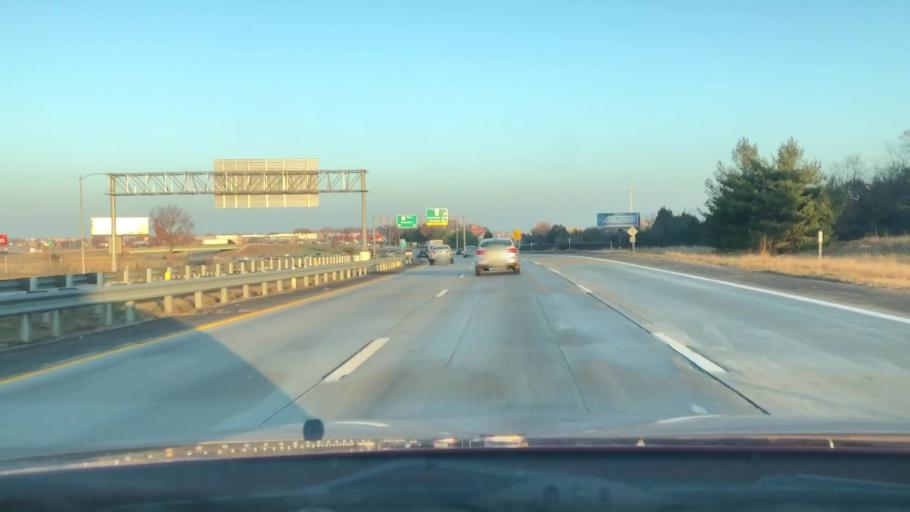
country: US
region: Missouri
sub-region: Greene County
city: Springfield
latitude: 37.1367
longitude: -93.2480
